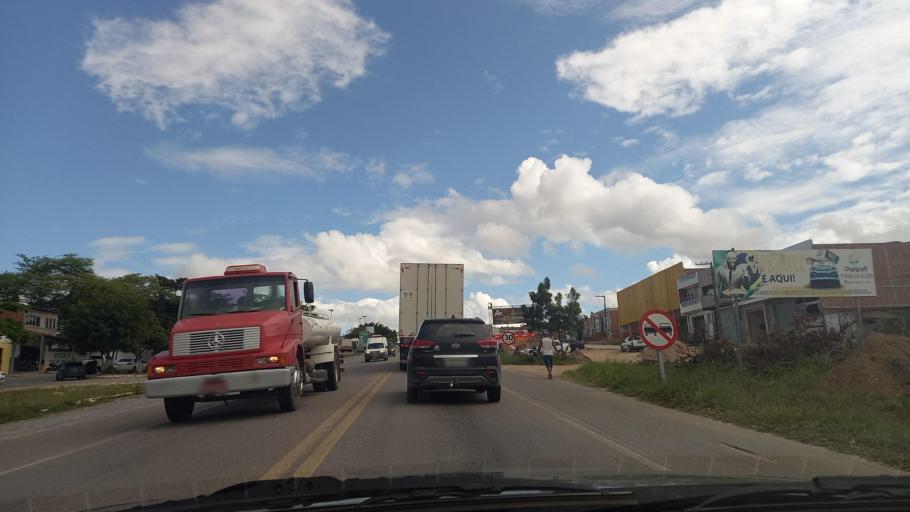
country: BR
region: Pernambuco
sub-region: Lajedo
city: Lajedo
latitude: -8.7087
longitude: -36.4188
